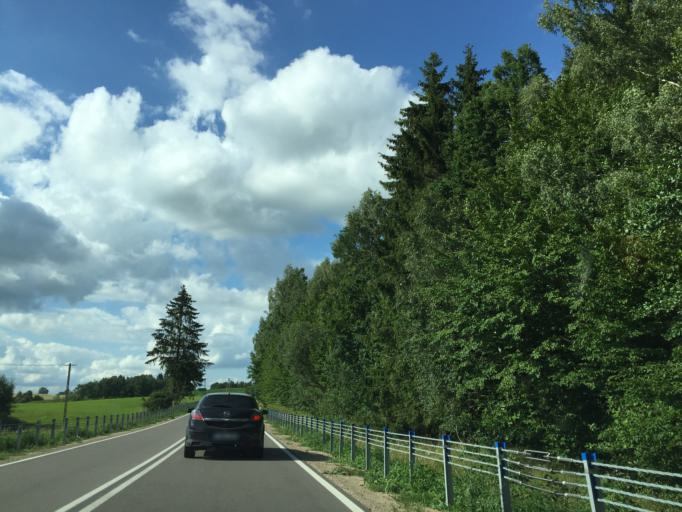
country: PL
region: Podlasie
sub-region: Powiat sejnenski
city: Punsk
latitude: 54.2393
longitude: 23.0986
